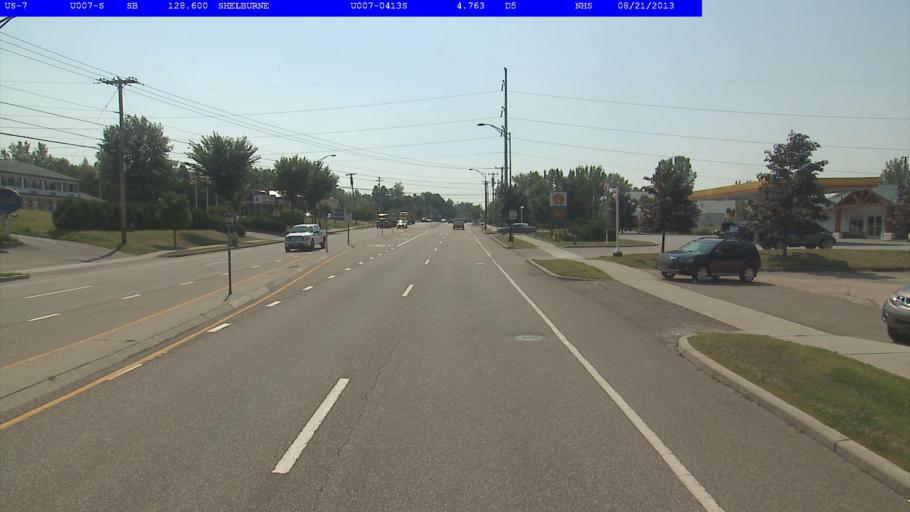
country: US
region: Vermont
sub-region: Chittenden County
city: Burlington
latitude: 44.4218
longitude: -73.2121
